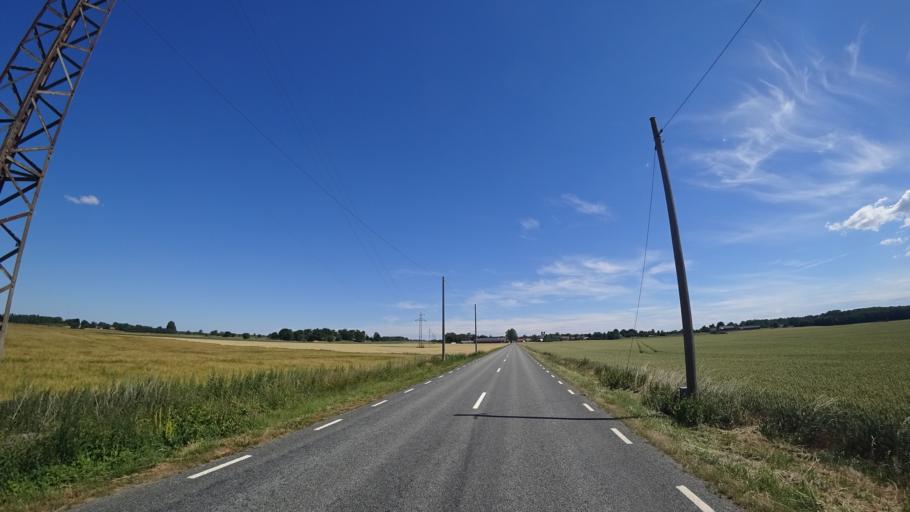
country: SE
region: Skane
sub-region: Kristianstads Kommun
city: Onnestad
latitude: 56.0696
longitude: 14.0664
